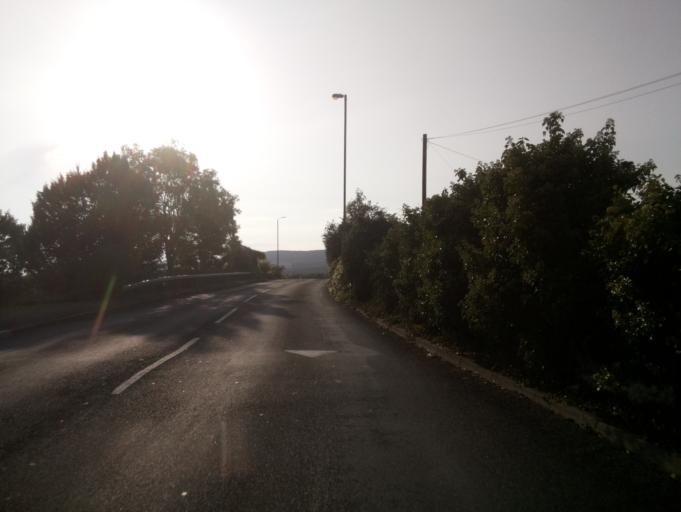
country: GB
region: Wales
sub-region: Torfaen County Borough
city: Cwmbran
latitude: 51.6600
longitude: -3.0157
